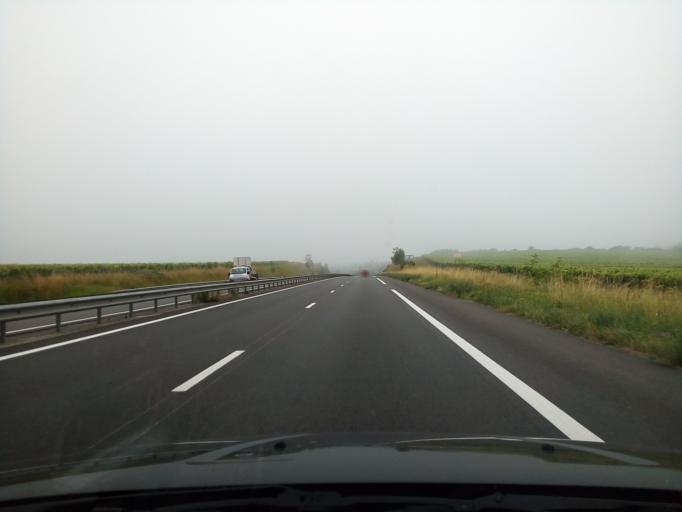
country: FR
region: Poitou-Charentes
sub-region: Departement de la Charente
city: Jarnac
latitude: 45.6688
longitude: -0.2030
